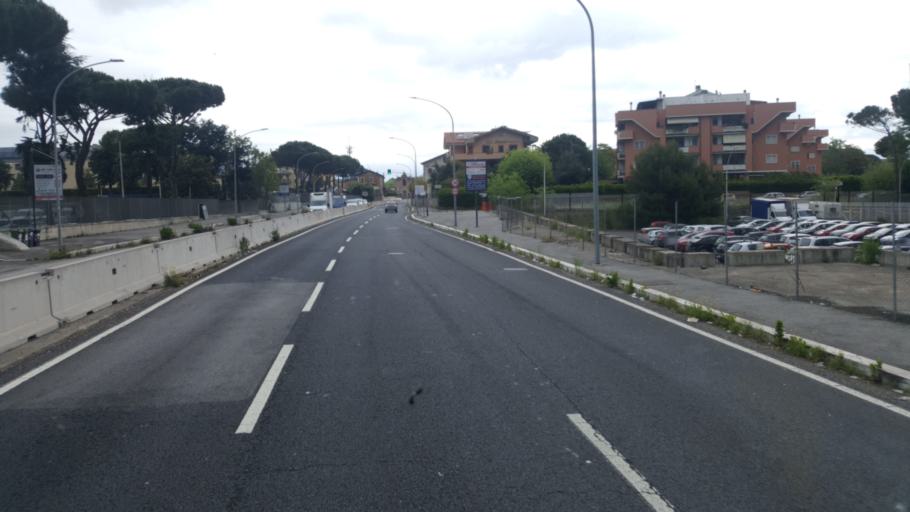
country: IT
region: Latium
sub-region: Citta metropolitana di Roma Capitale
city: Setteville
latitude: 41.9371
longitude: 12.6180
